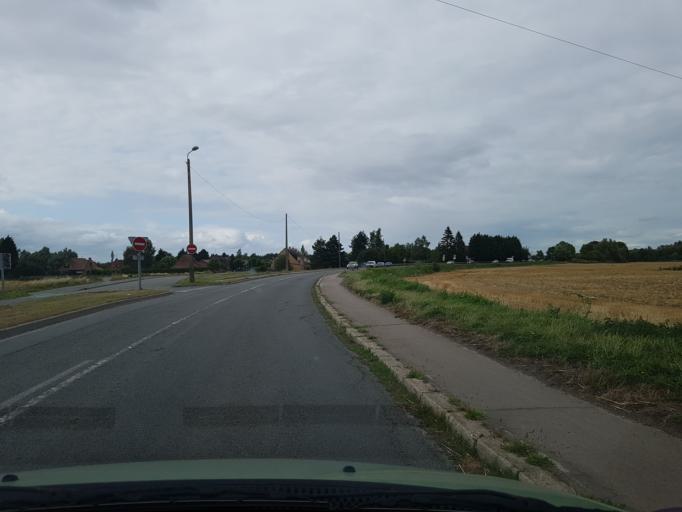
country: FR
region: Nord-Pas-de-Calais
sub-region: Departement du Nord
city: Don
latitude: 50.5407
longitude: 2.9204
